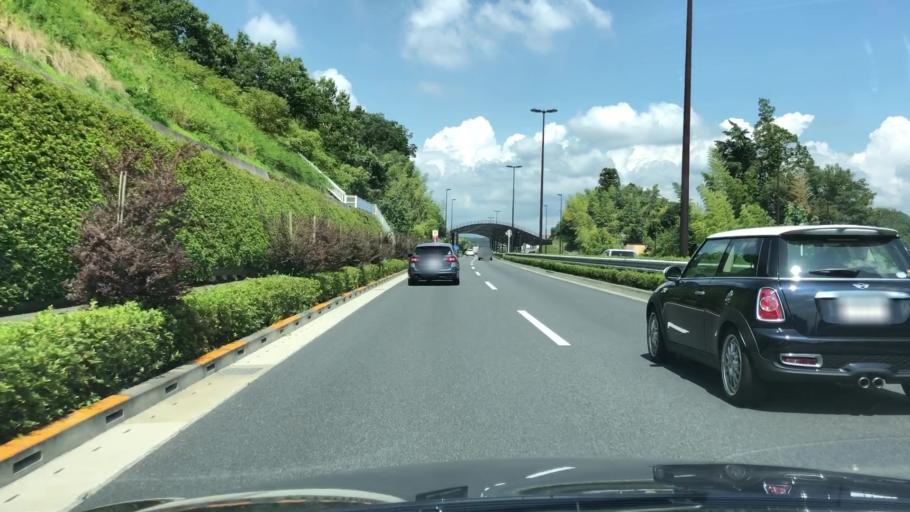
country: JP
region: Tokyo
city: Fussa
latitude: 35.7002
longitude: 139.3117
